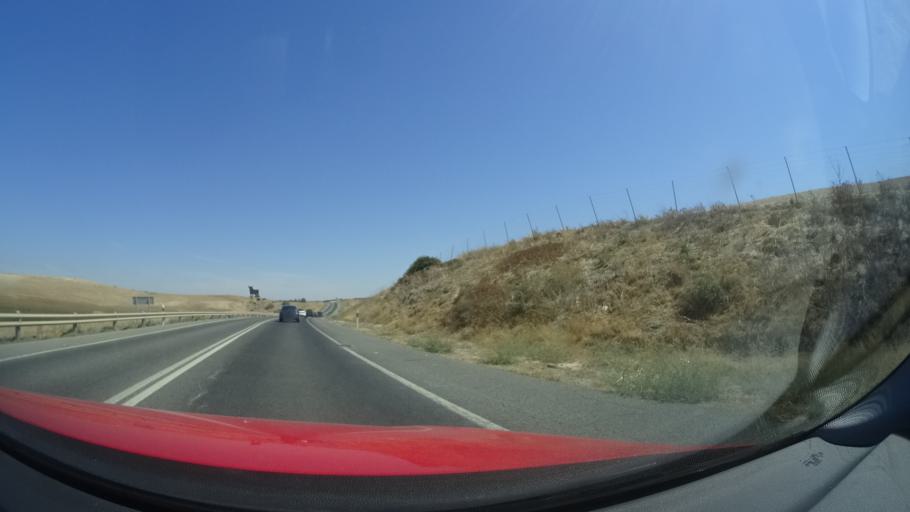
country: ES
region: Andalusia
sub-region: Provincia de Sevilla
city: Las Cabezas de San Juan
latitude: 36.9637
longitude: -5.8822
